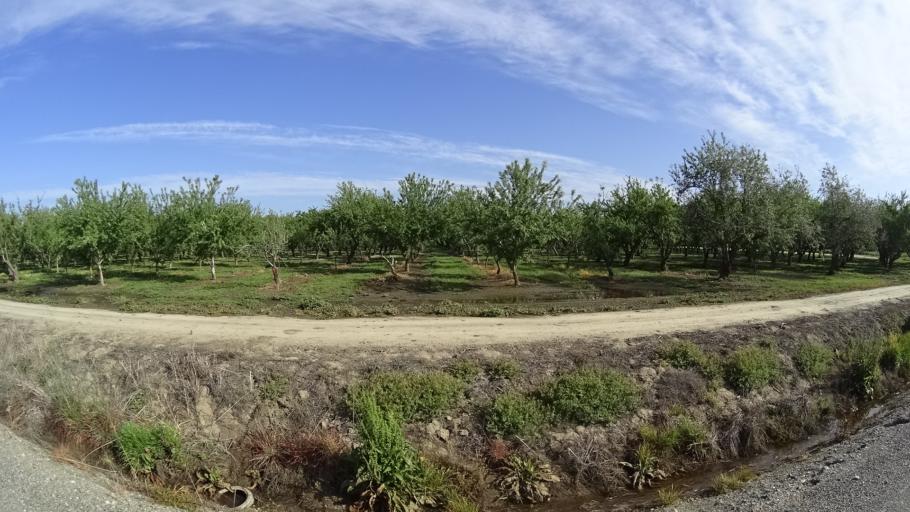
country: US
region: California
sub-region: Glenn County
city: Hamilton City
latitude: 39.6306
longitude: -122.0213
